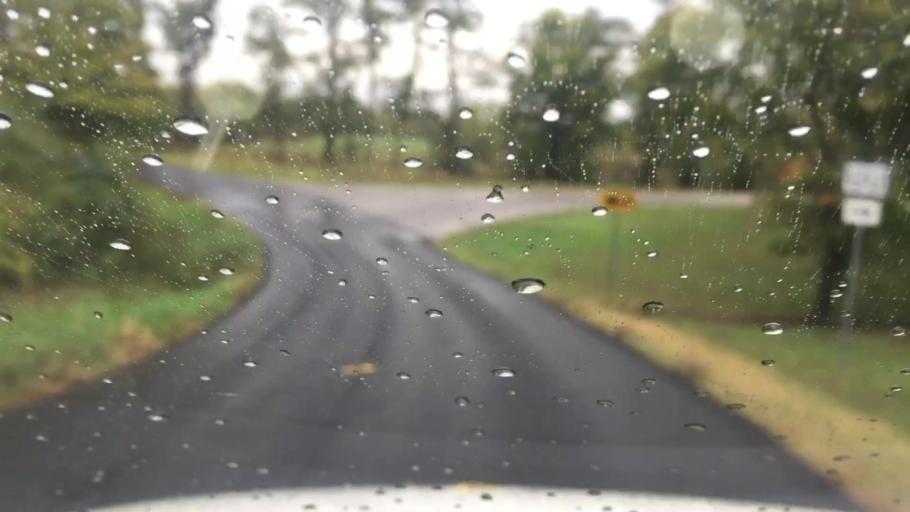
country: US
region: Missouri
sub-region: Boone County
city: Columbia
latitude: 38.9350
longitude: -92.4697
